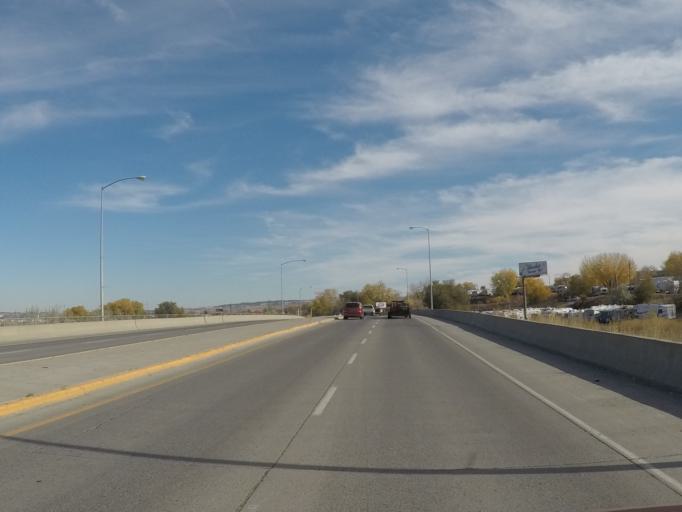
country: US
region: Montana
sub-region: Yellowstone County
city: Billings
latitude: 45.7961
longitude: -108.4667
